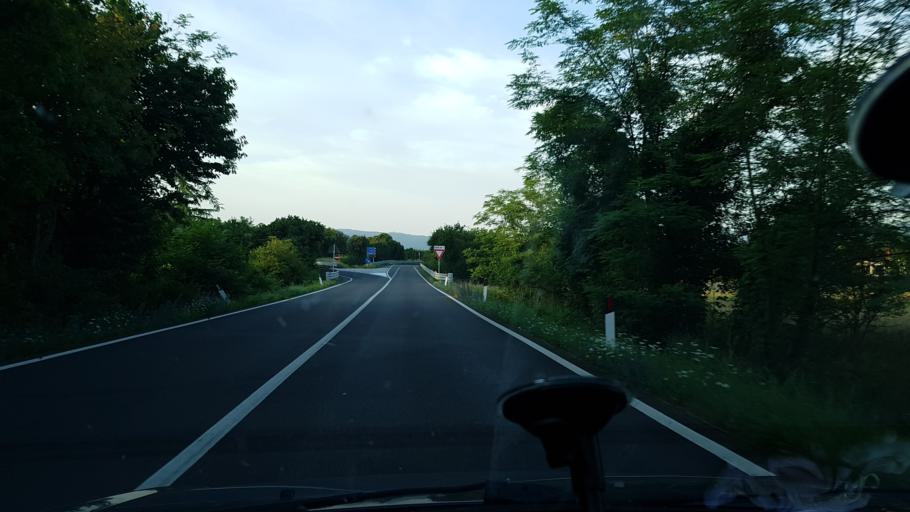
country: IT
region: Friuli Venezia Giulia
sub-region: Provincia di Gorizia
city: Savogna d'Isonzo
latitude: 45.9213
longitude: 13.5719
